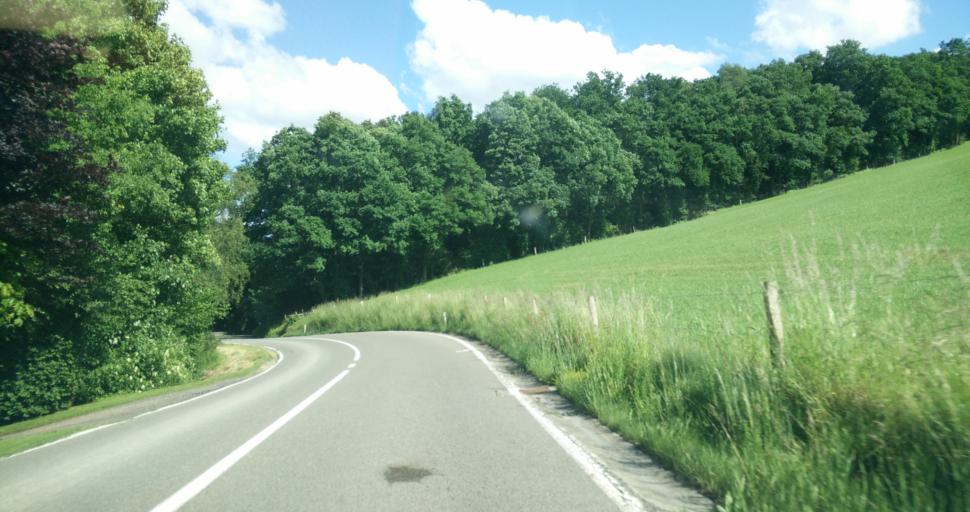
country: BE
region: Wallonia
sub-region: Province du Luxembourg
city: Rendeux
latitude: 50.1878
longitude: 5.5101
